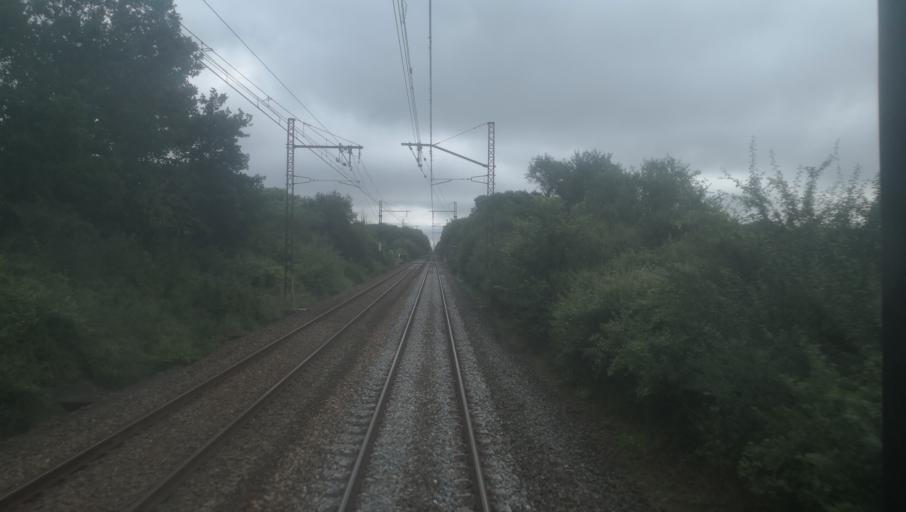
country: FR
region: Centre
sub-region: Departement de l'Indre
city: Montierchaume
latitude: 46.8459
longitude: 1.7830
